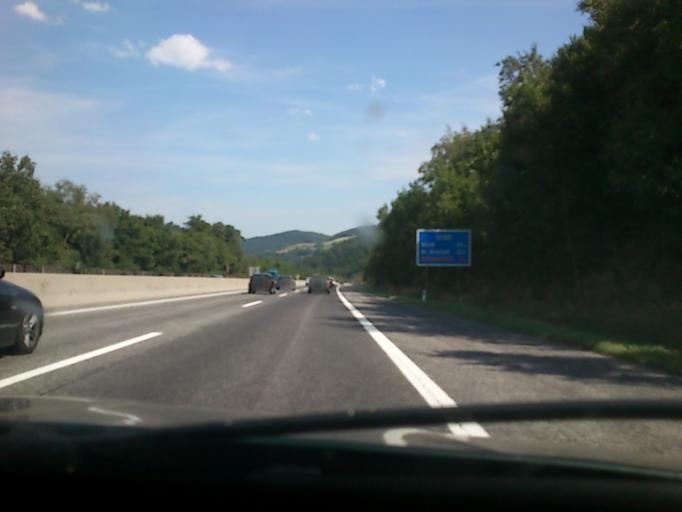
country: AT
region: Lower Austria
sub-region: Politischer Bezirk Neunkirchen
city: Grimmenstein
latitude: 47.6155
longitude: 16.1302
